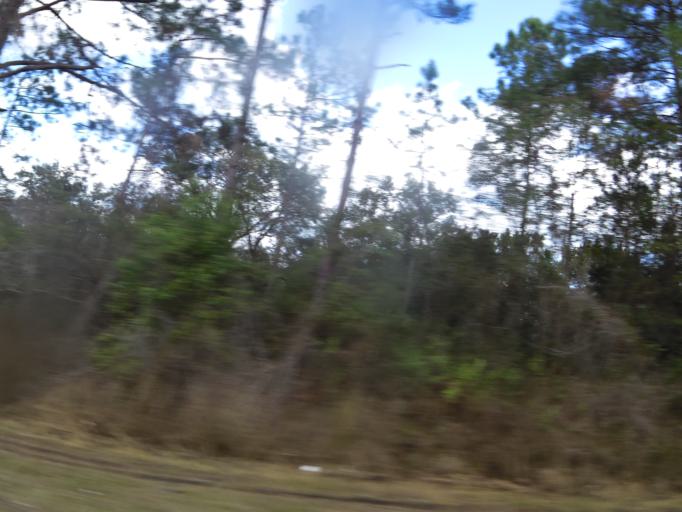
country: US
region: Florida
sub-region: Volusia County
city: Pierson
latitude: 29.2006
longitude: -81.4377
